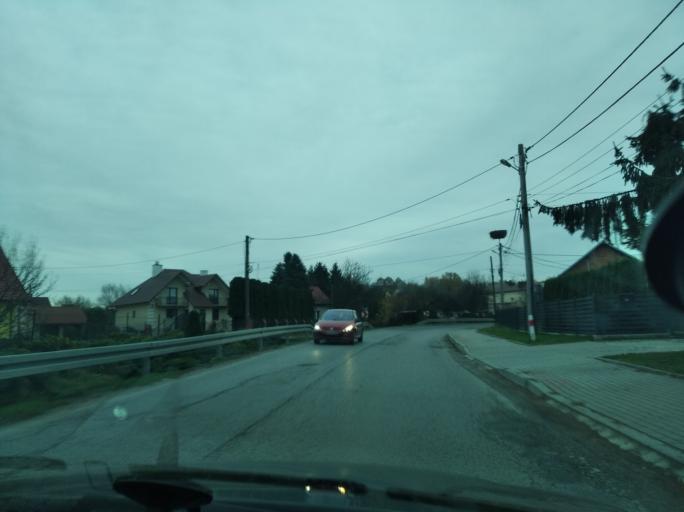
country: PL
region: Subcarpathian Voivodeship
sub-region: Powiat lancucki
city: Krzemienica
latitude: 50.0792
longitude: 22.1903
